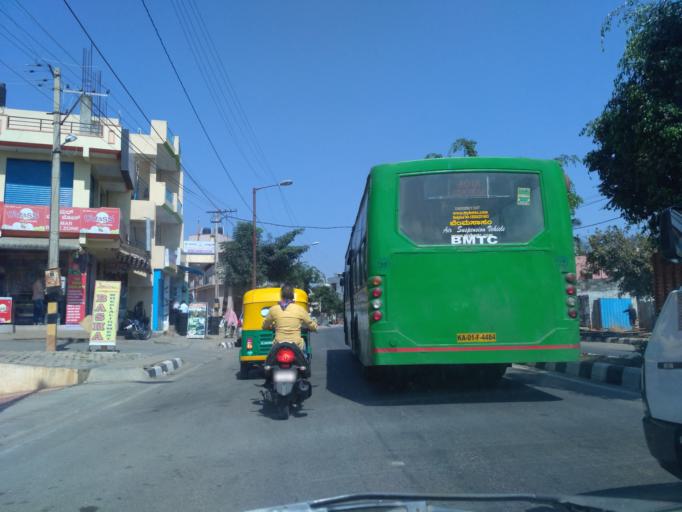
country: IN
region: Karnataka
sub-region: Bangalore Urban
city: Yelahanka
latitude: 13.0850
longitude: 77.5532
